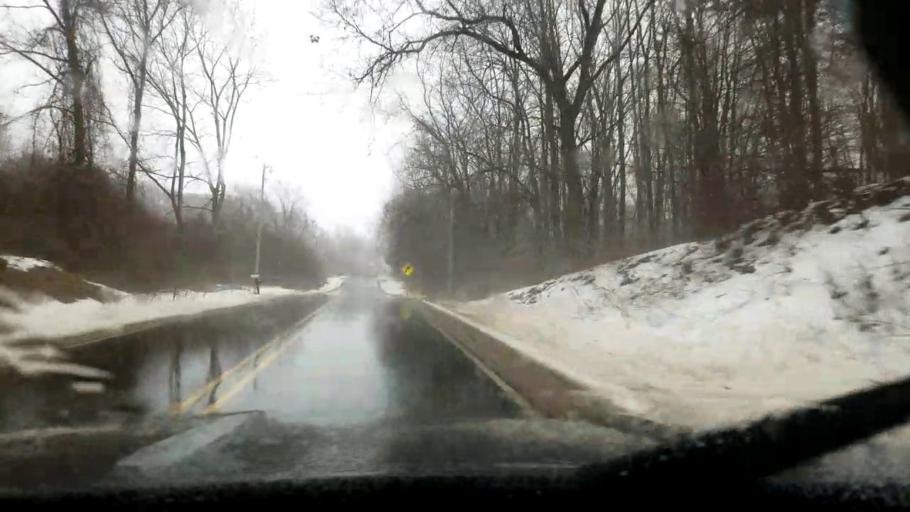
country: US
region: Michigan
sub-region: Jackson County
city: Grass Lake
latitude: 42.3355
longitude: -84.1593
